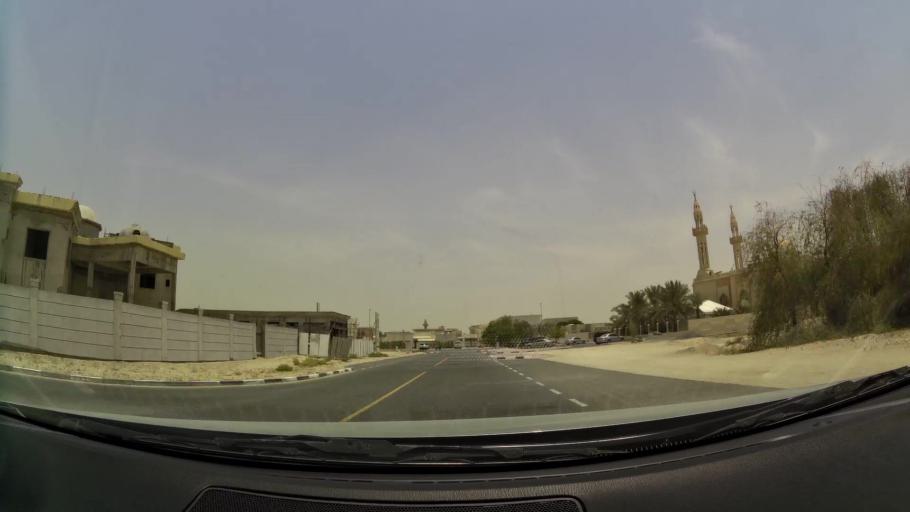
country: AE
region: Ash Shariqah
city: Sharjah
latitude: 25.2072
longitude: 55.3796
